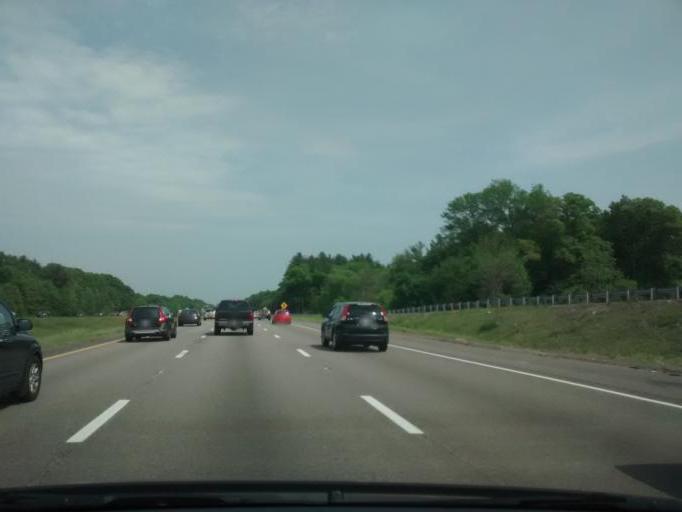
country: US
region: Massachusetts
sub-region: Bristol County
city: Mansfield Center
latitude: 42.0001
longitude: -71.2098
